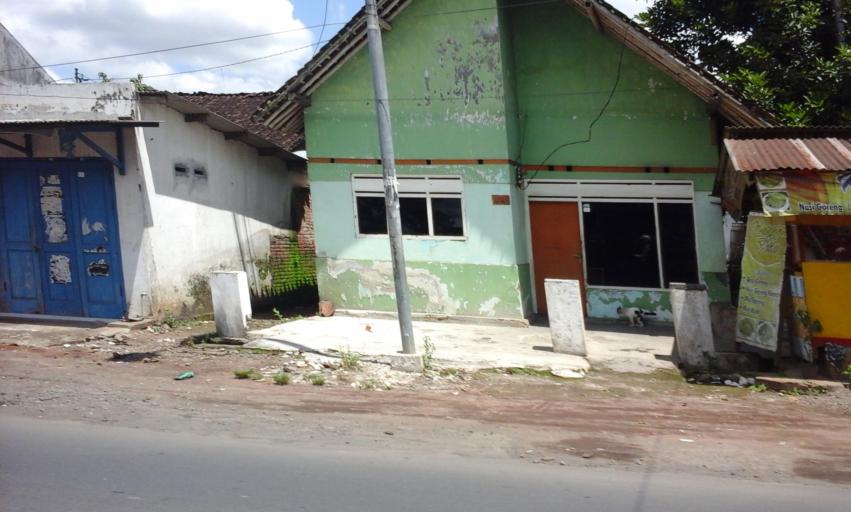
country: ID
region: East Java
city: Sumberketangi
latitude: -8.1865
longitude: 113.7335
